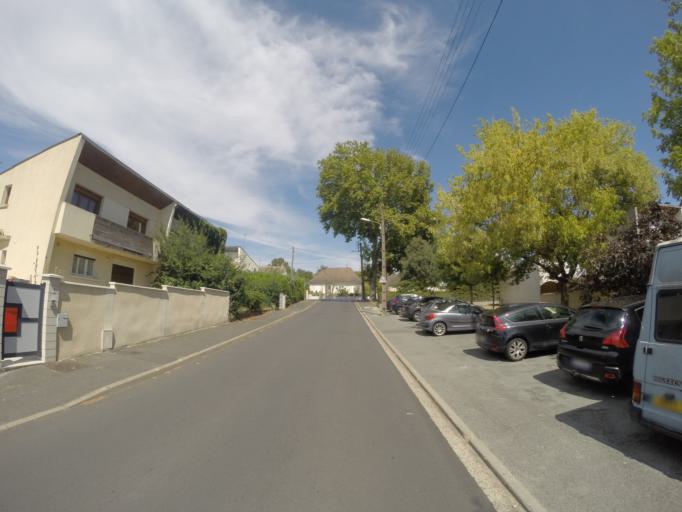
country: FR
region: Centre
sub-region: Departement d'Indre-et-Loire
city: Tours
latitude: 47.4091
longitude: 0.7141
